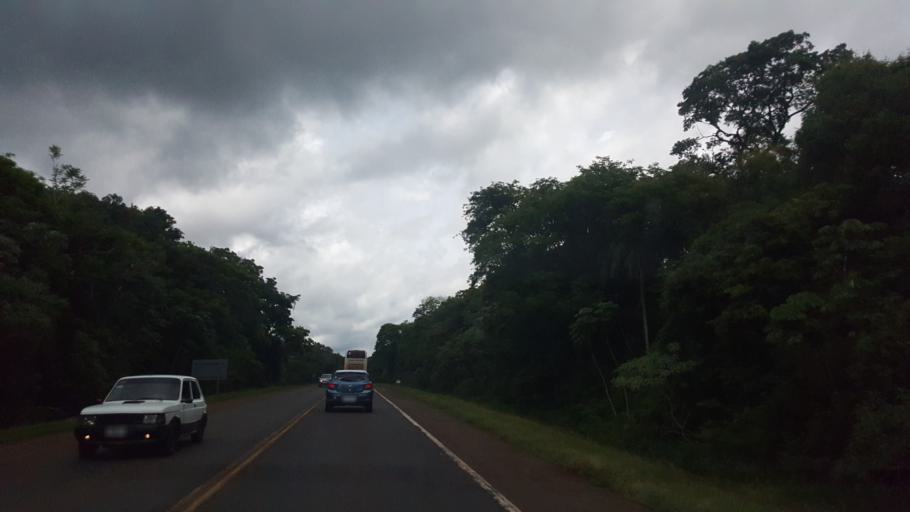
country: AR
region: Misiones
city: Puerto Libertad
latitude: -25.8013
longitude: -54.5382
